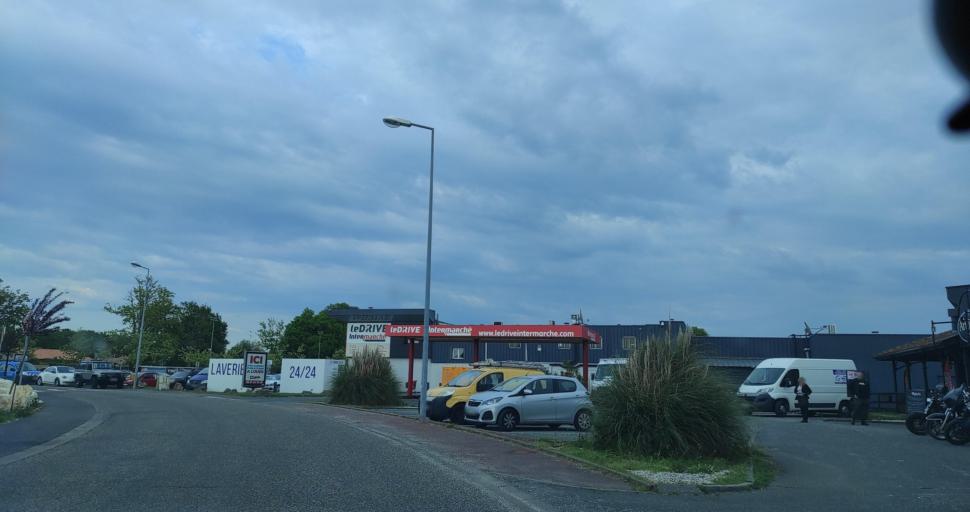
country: FR
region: Aquitaine
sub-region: Departement de la Gironde
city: Lanton
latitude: 44.7026
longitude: -1.0399
